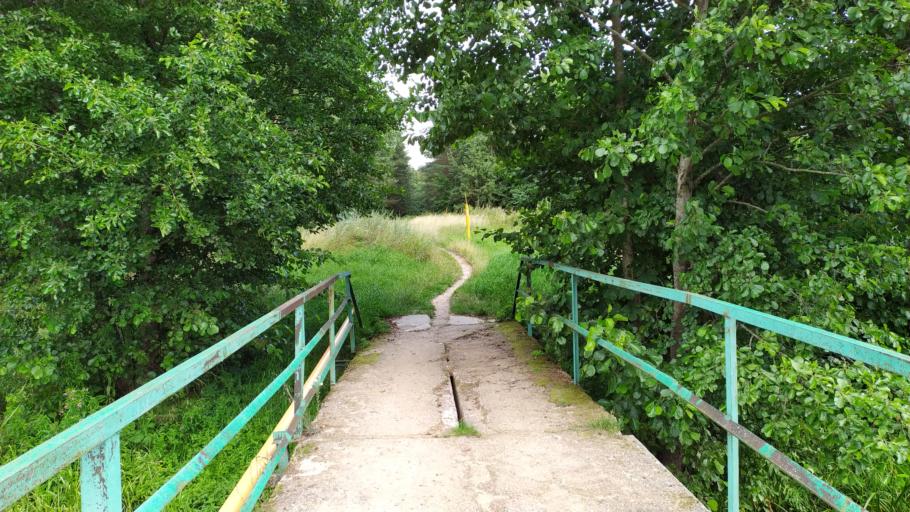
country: BY
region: Minsk
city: Krupki
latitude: 54.3266
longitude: 29.1521
